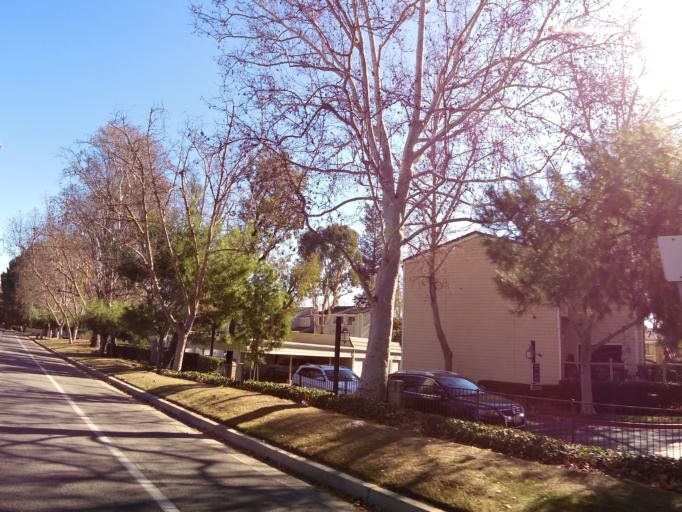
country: US
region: California
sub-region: Ventura County
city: Thousand Oaks
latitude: 34.1498
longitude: -118.8348
